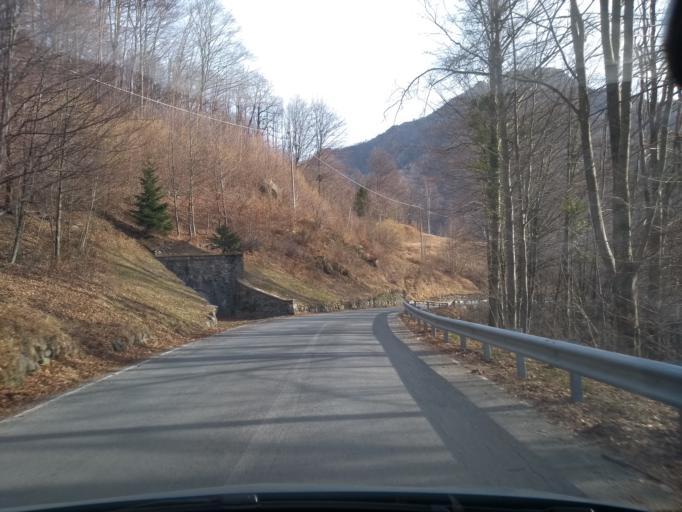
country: IT
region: Piedmont
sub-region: Provincia di Torino
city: Ala di Stura
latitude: 45.3136
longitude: 7.3146
